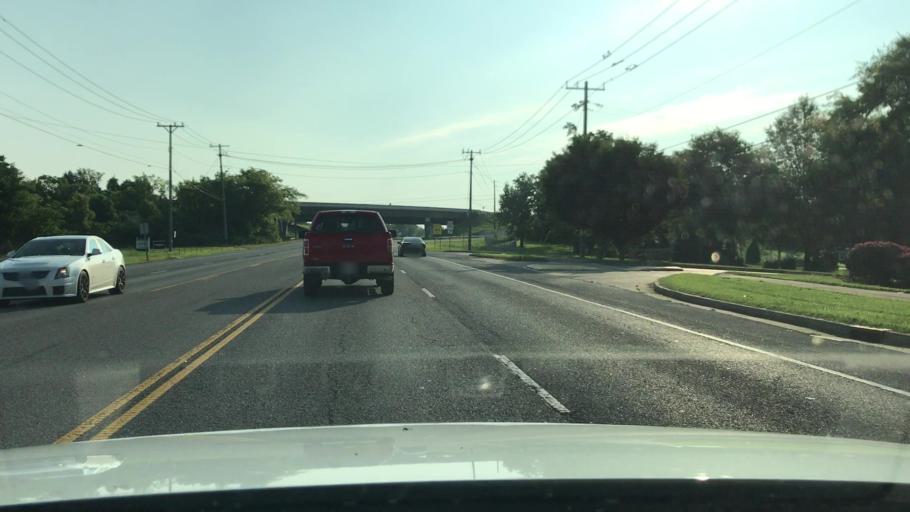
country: US
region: Tennessee
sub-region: Sumner County
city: Hendersonville
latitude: 36.3272
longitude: -86.5614
